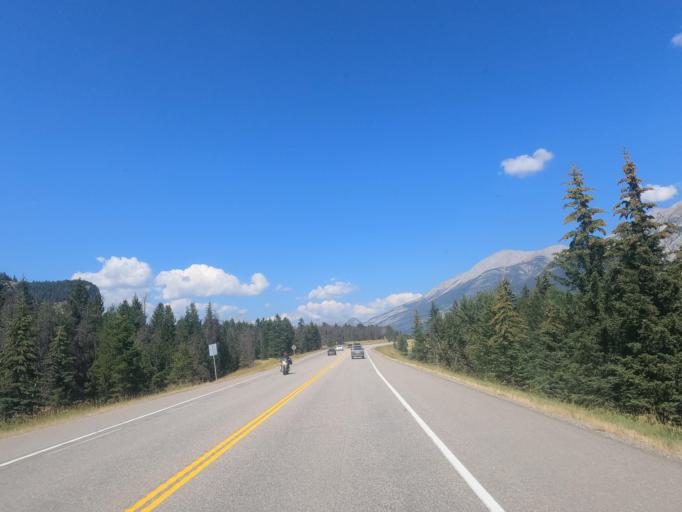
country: CA
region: Alberta
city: Jasper Park Lodge
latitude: 52.9373
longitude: -118.0390
